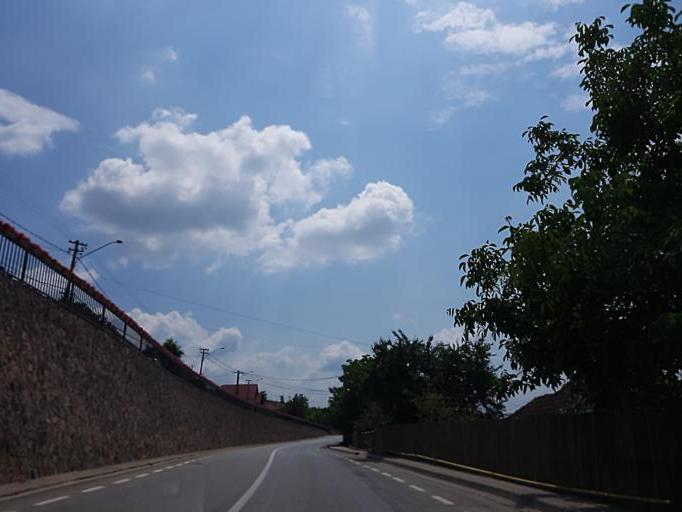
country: RO
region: Alba
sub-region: Municipiul Blaj
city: Veza
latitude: 46.1719
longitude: 23.9415
